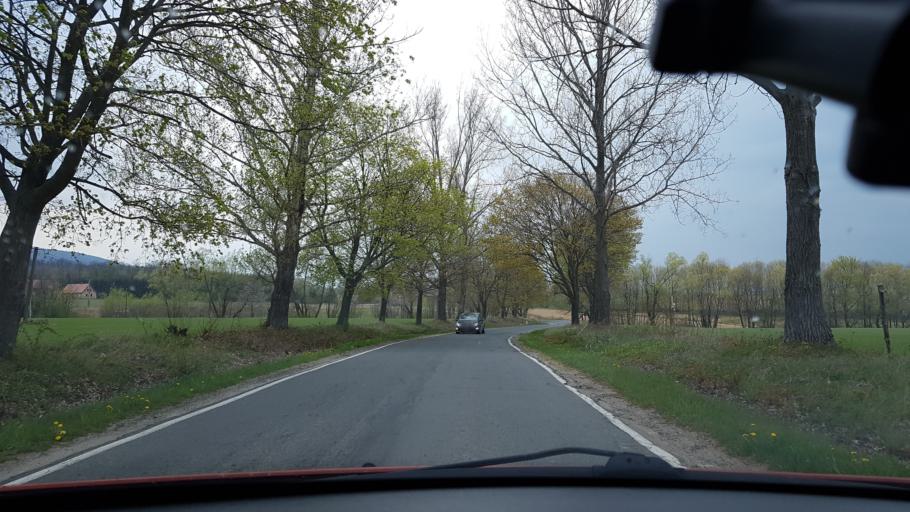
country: PL
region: Lower Silesian Voivodeship
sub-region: Powiat klodzki
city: Bystrzyca Klodzka
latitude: 50.3325
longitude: 16.6007
